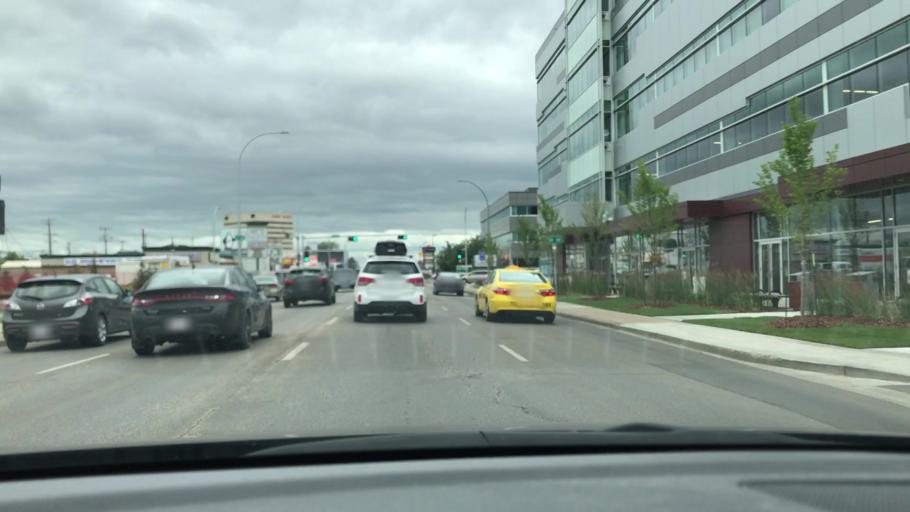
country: CA
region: Alberta
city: Edmonton
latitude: 53.4989
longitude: -113.4977
